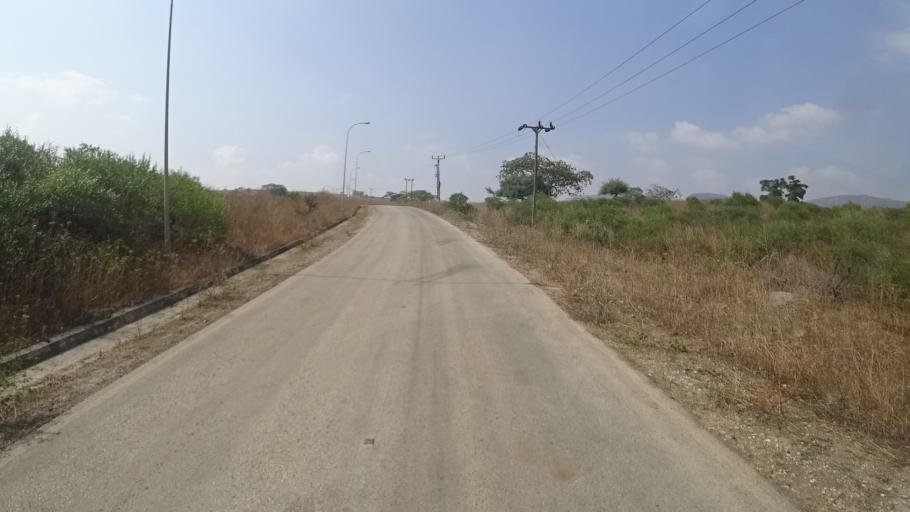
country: YE
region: Al Mahrah
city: Hawf
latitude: 16.7294
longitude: 53.2735
